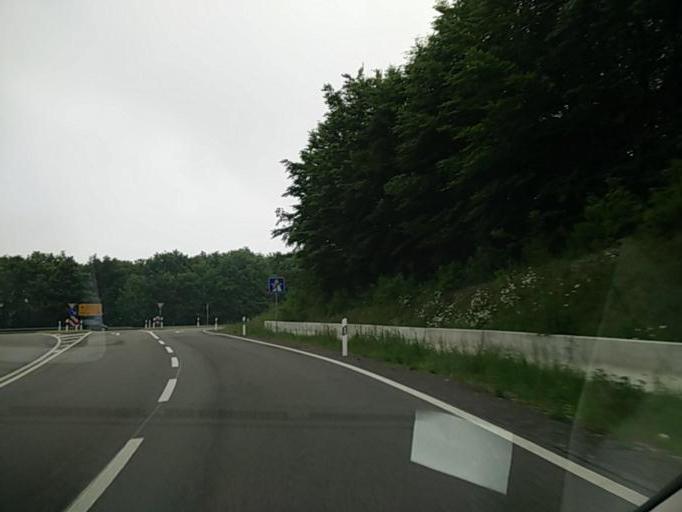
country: DE
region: Baden-Wuerttemberg
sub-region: Regierungsbezirk Stuttgart
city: Ehningen
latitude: 48.6670
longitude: 8.9649
